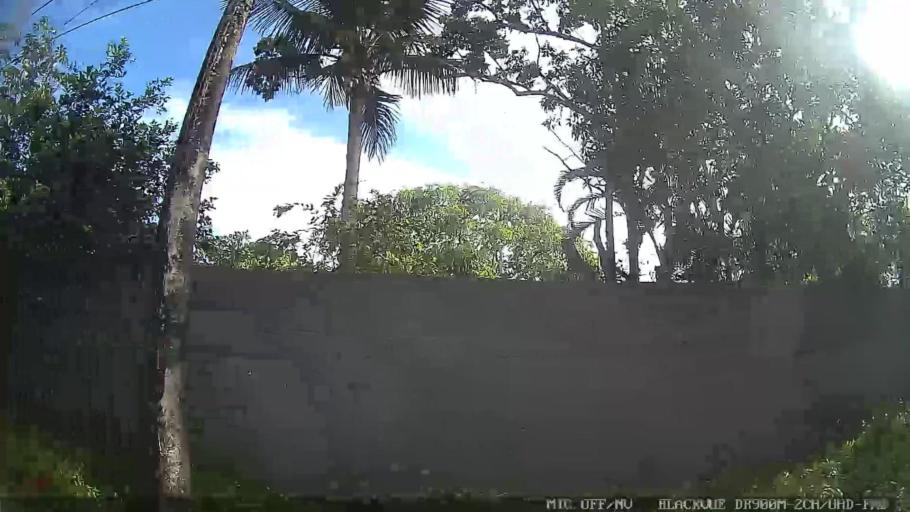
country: BR
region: Sao Paulo
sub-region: Itanhaem
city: Itanhaem
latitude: -24.2015
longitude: -46.8900
